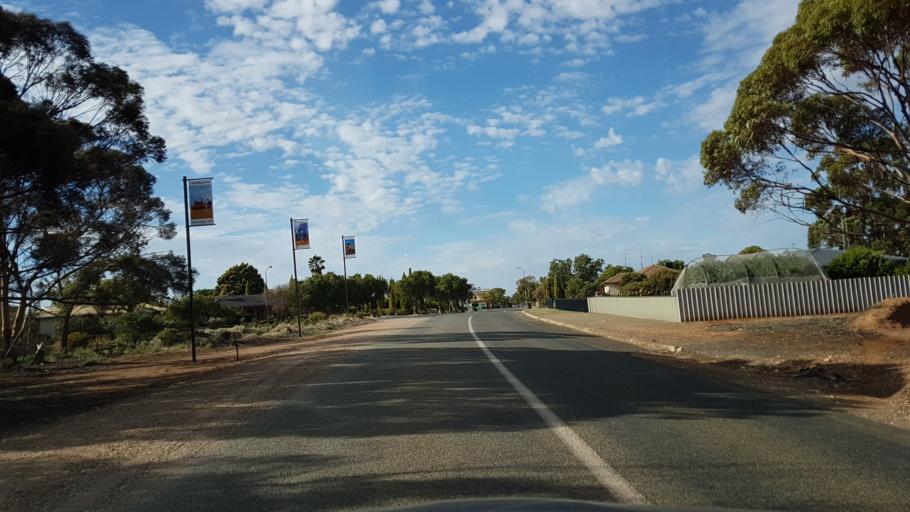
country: AU
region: South Australia
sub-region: Clare and Gilbert Valleys
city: Clare
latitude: -33.8429
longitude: 138.4878
